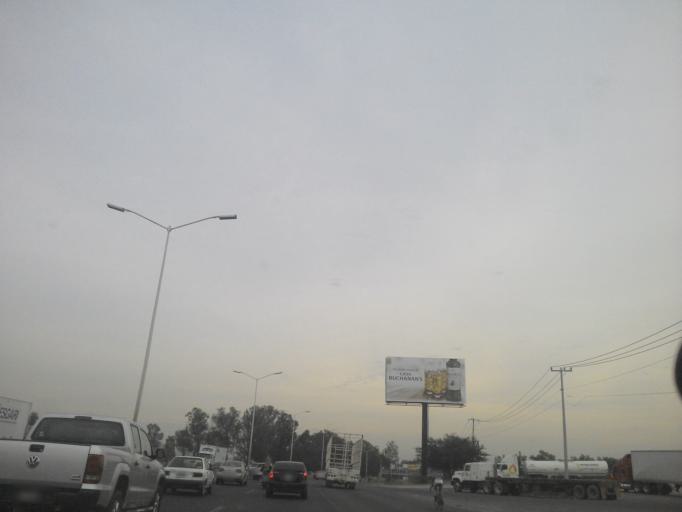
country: MX
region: Jalisco
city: Guadalajara
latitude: 20.6698
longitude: -103.4528
